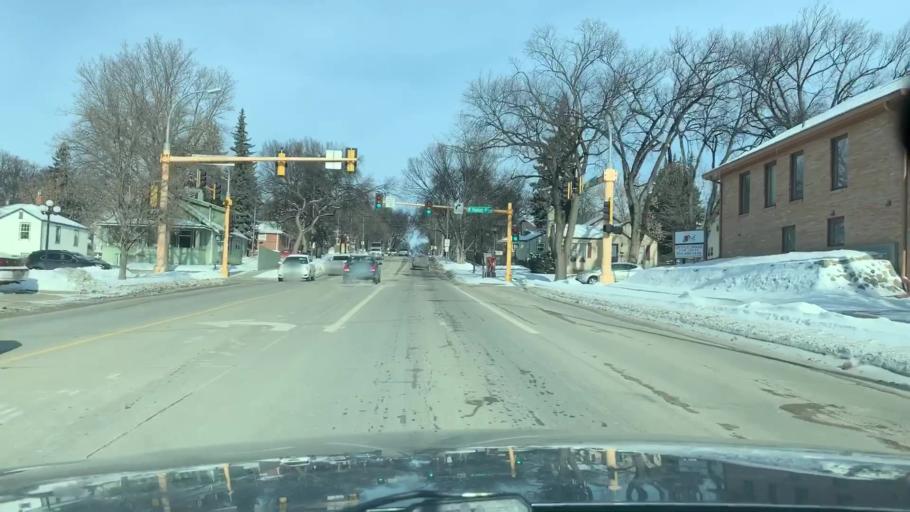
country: US
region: North Dakota
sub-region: Burleigh County
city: Bismarck
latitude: 46.8083
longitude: -100.7943
